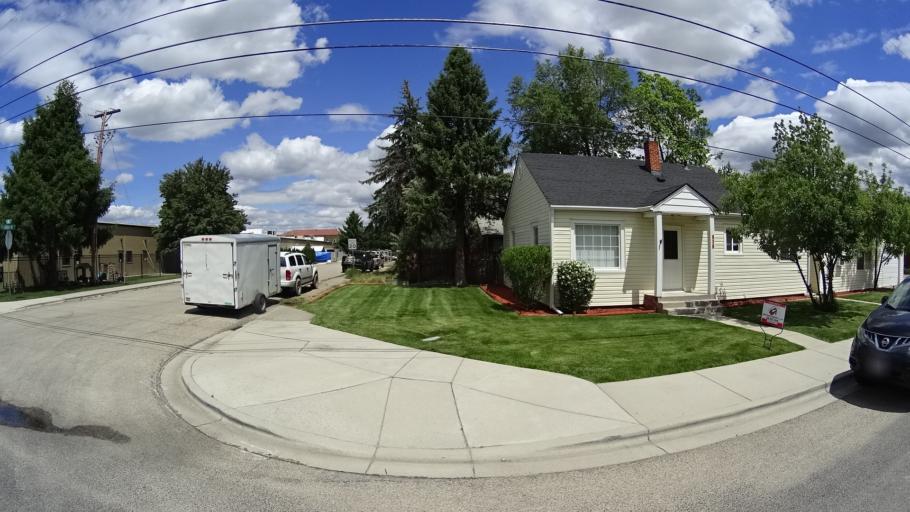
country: US
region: Idaho
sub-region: Ada County
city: Boise
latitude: 43.5844
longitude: -116.1921
